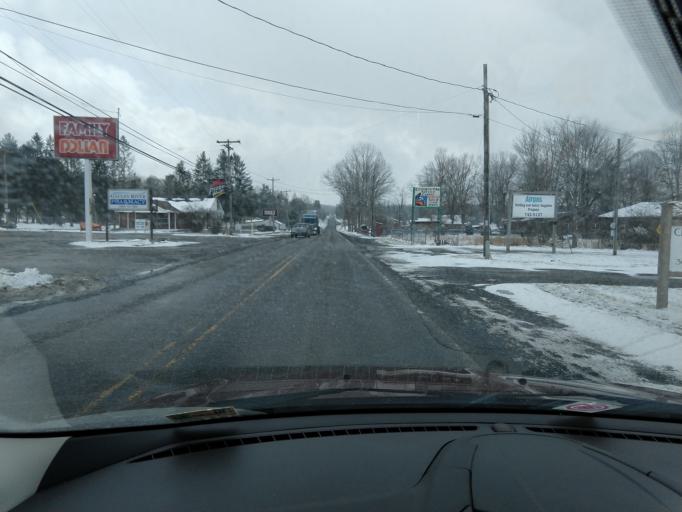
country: US
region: West Virginia
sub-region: Nicholas County
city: Craigsville
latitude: 38.3248
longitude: -80.6537
